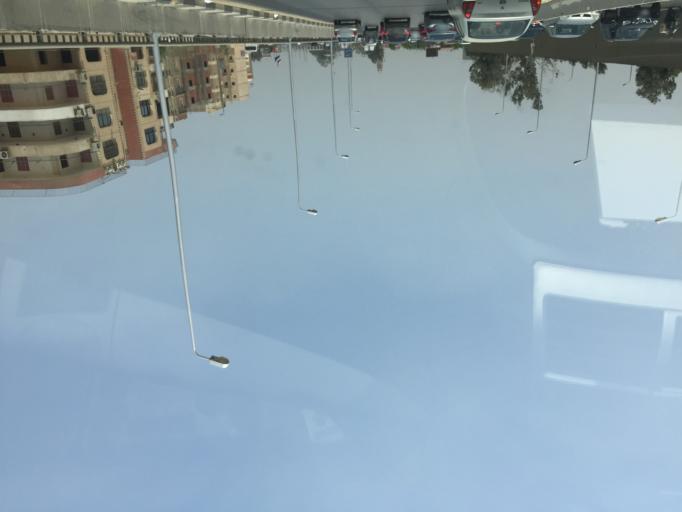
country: EG
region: Muhafazat al Qahirah
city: Cairo
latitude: 30.0789
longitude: 31.3775
